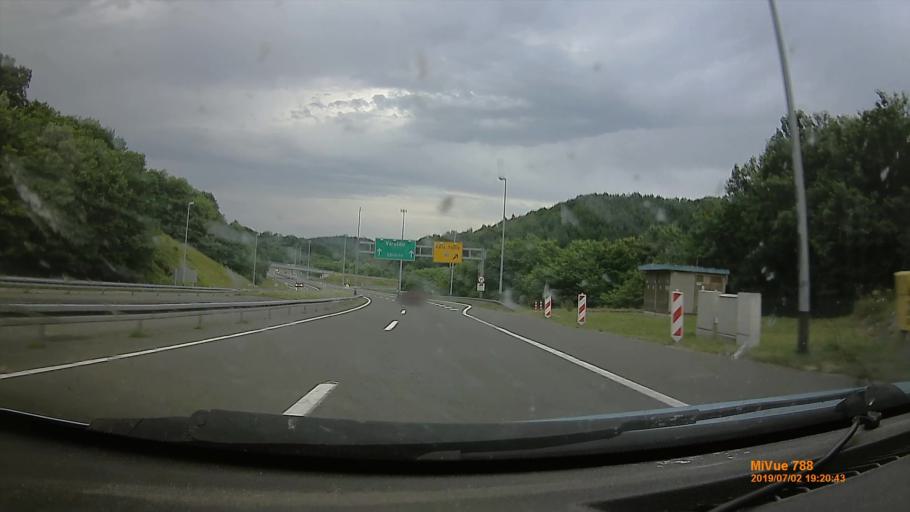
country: HR
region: Varazdinska
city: Ljubescica
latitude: 46.2069
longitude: 16.4109
